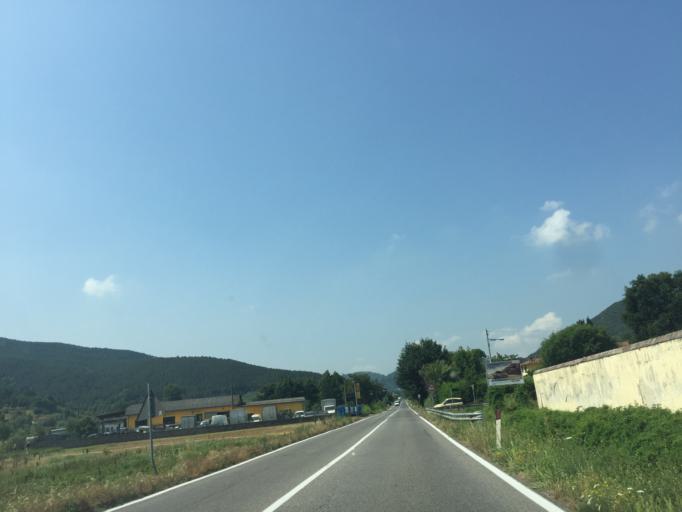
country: IT
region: Tuscany
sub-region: Province of Pisa
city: Asciano
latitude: 43.7958
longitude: 10.4806
